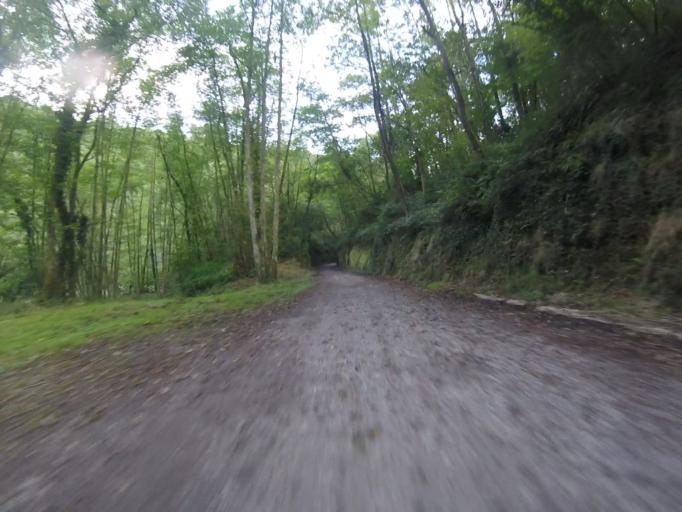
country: ES
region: Basque Country
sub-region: Provincia de Guipuzcoa
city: Berastegui
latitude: 43.1659
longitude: -1.9637
